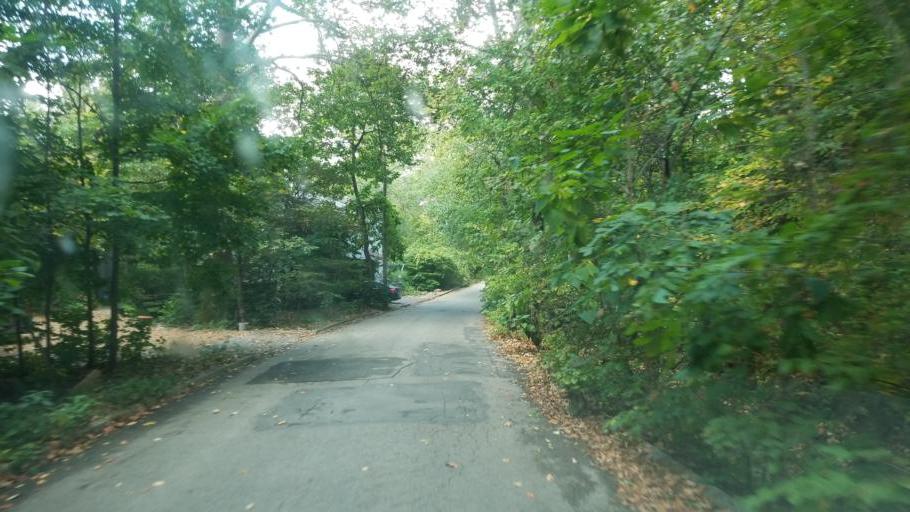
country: US
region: Ohio
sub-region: Franklin County
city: Grandview Heights
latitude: 40.0250
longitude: -83.0119
